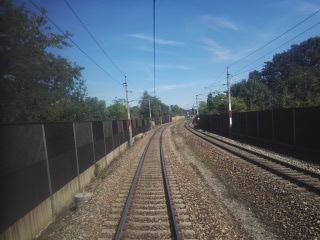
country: AT
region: Upper Austria
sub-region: Politischer Bezirk Grieskirchen
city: Bad Schallerbach
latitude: 48.2295
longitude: 13.9155
